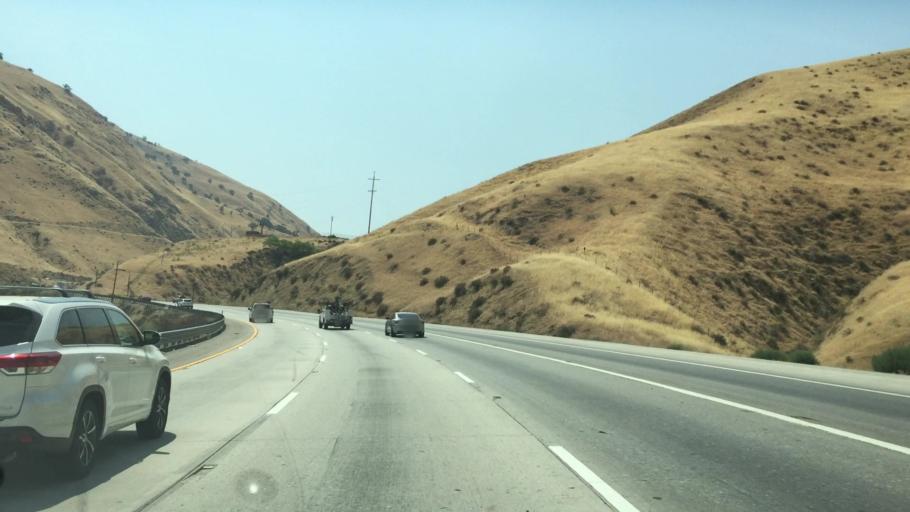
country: US
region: California
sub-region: Kern County
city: Frazier Park
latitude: 34.9253
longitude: -118.9286
